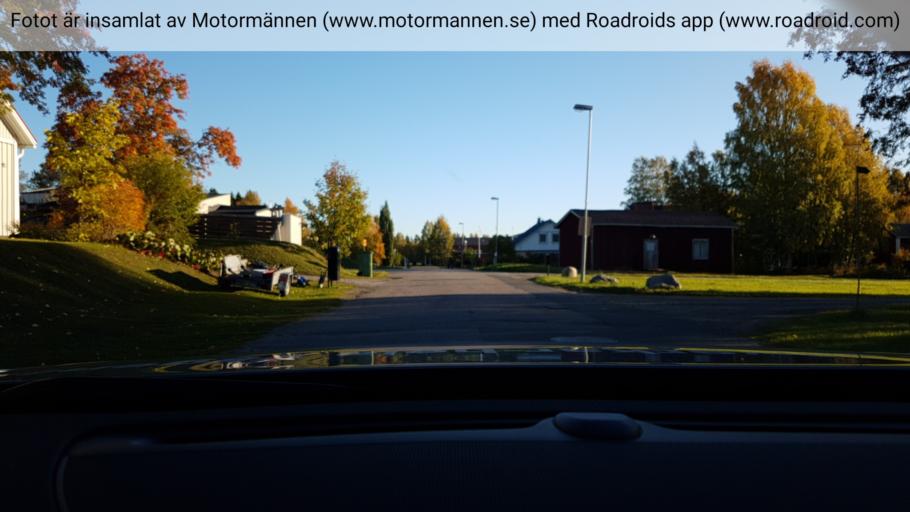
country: SE
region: Norrbotten
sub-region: Lulea Kommun
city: Sodra Sunderbyn
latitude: 65.6581
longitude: 21.9444
